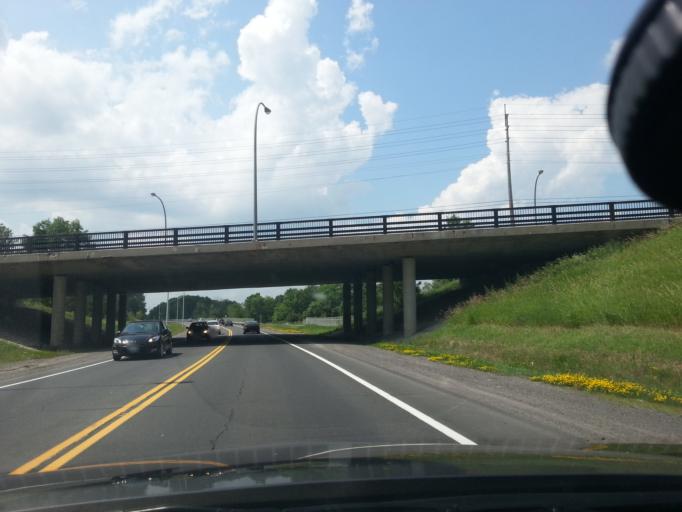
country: CA
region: Ontario
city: Ottawa
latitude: 45.3680
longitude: -75.6681
